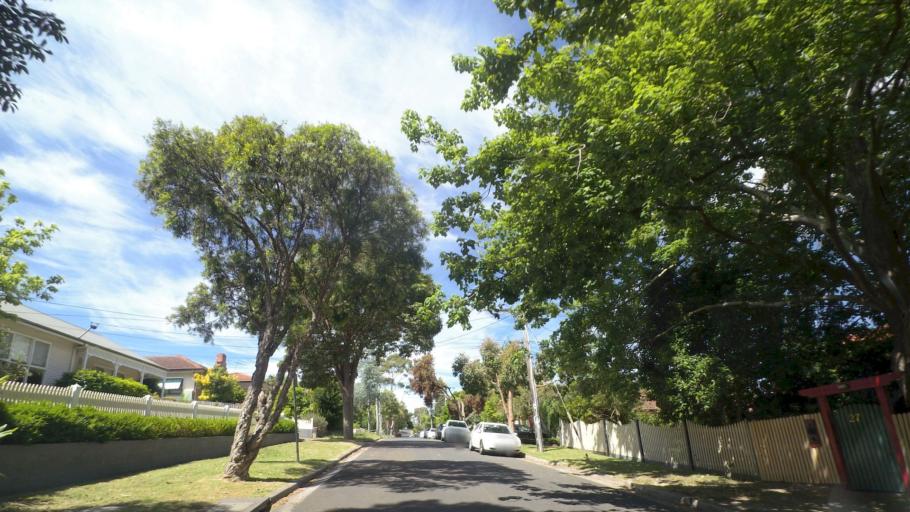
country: AU
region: Victoria
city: Mitcham
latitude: -37.8092
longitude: 145.2221
